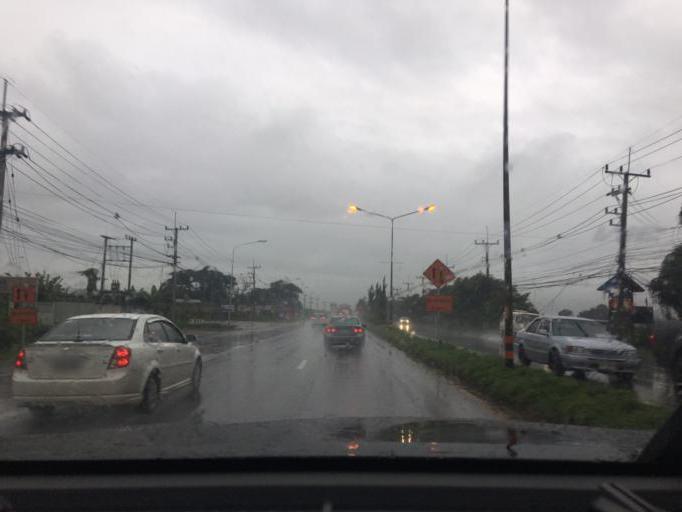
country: TH
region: Chiang Rai
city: Mae Chan
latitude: 20.0320
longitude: 99.8742
